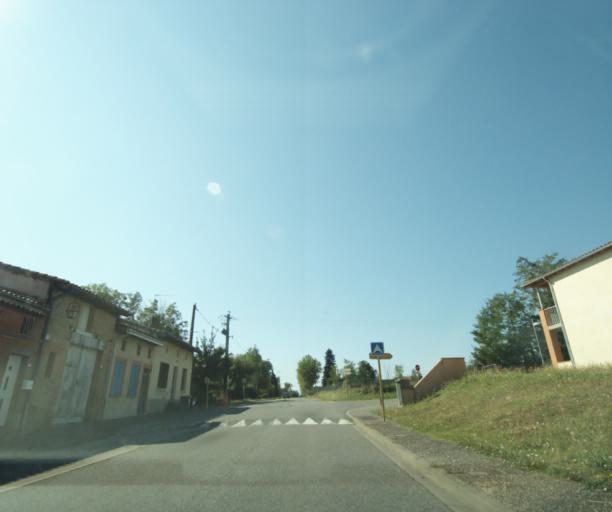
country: FR
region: Midi-Pyrenees
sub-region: Departement de la Haute-Garonne
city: Saint-Sulpice-sur-Leze
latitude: 43.3246
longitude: 1.3224
